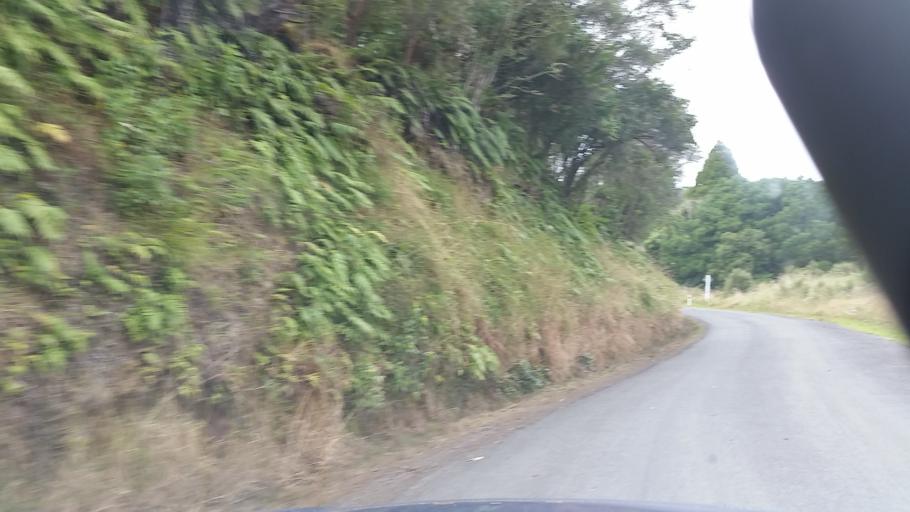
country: NZ
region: Taranaki
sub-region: South Taranaki District
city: Eltham
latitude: -39.3262
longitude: 174.6163
